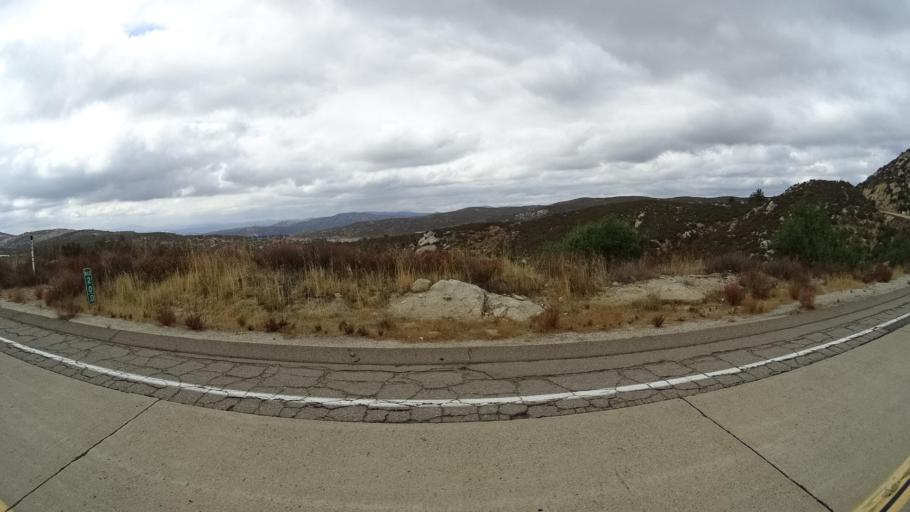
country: US
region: California
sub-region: San Diego County
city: Campo
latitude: 32.7081
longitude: -116.3812
